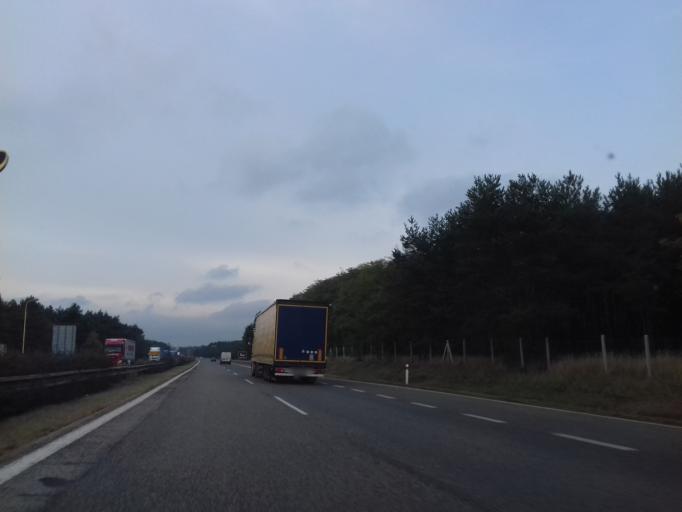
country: AT
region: Lower Austria
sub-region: Politischer Bezirk Mistelbach
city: Rabensburg
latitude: 48.6161
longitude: 17.0123
